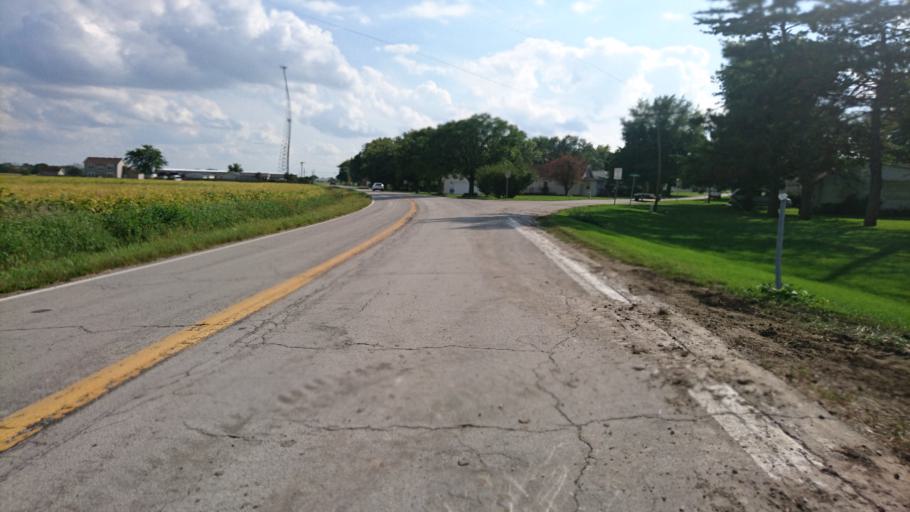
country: US
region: Illinois
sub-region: Logan County
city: Atlanta
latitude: 40.3175
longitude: -89.1658
